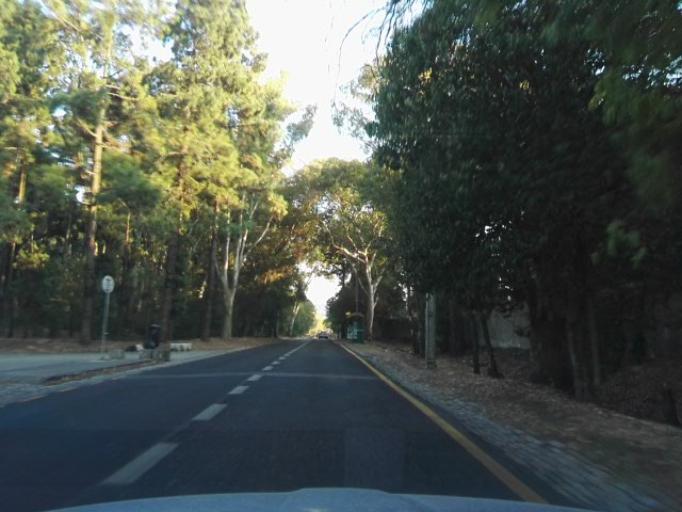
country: PT
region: Setubal
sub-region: Almada
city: Pragal
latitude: 38.7171
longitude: -9.1840
